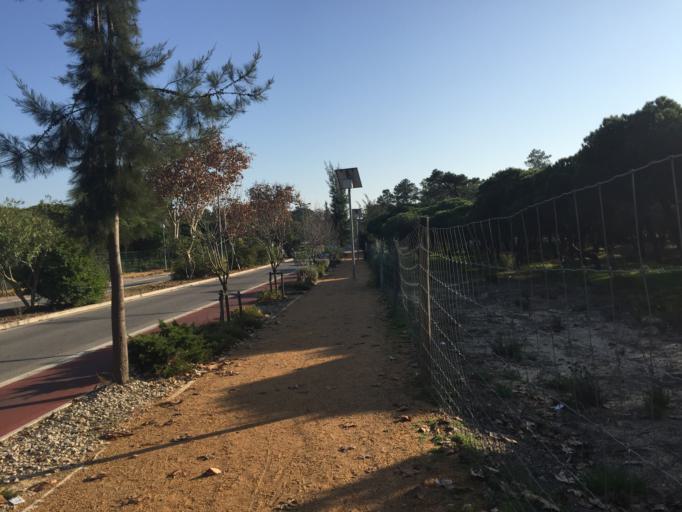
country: PT
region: Faro
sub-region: Vila Real de Santo Antonio
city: Vila Real de Santo Antonio
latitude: 37.1894
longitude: -7.4234
